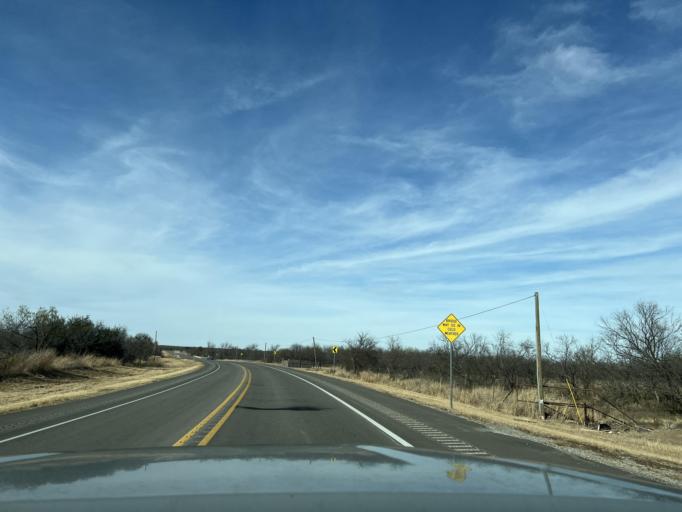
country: US
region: Texas
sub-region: Shackelford County
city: Albany
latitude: 32.6205
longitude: -99.2181
